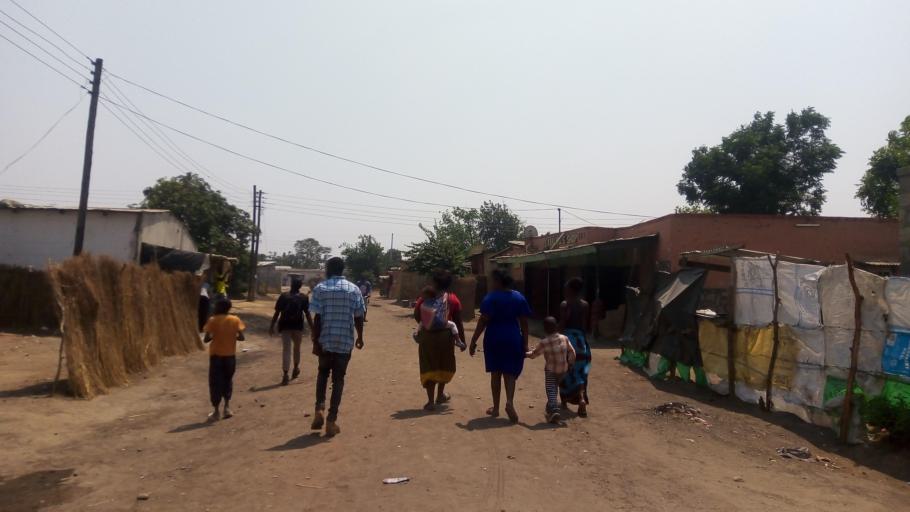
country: ZM
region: Lusaka
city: Lusaka
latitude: -15.4419
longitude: 28.3800
